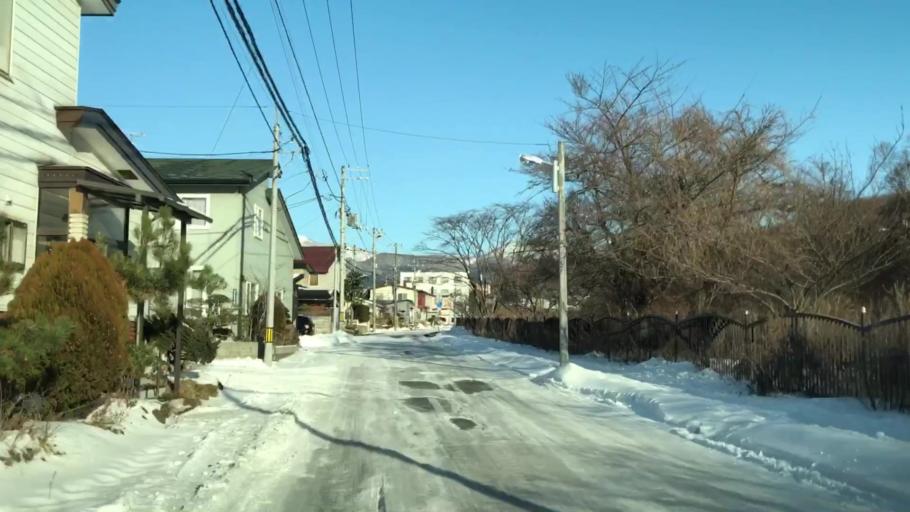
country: JP
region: Hokkaido
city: Muroran
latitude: 42.3737
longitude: 141.0378
